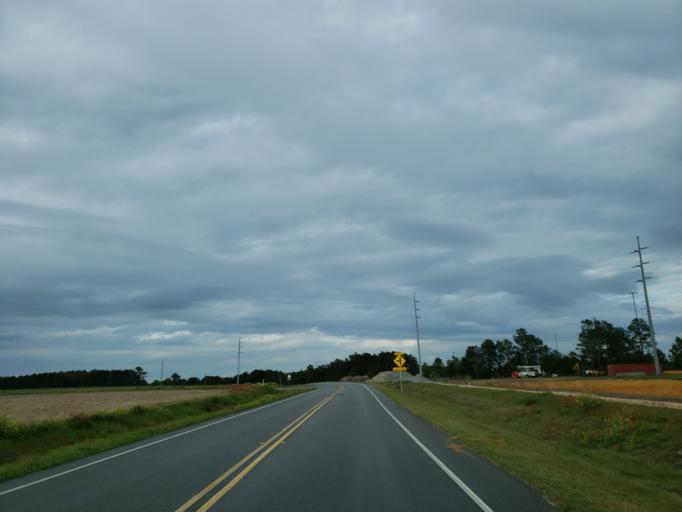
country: US
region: Georgia
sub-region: Dooly County
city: Vienna
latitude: 32.1258
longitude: -83.7634
